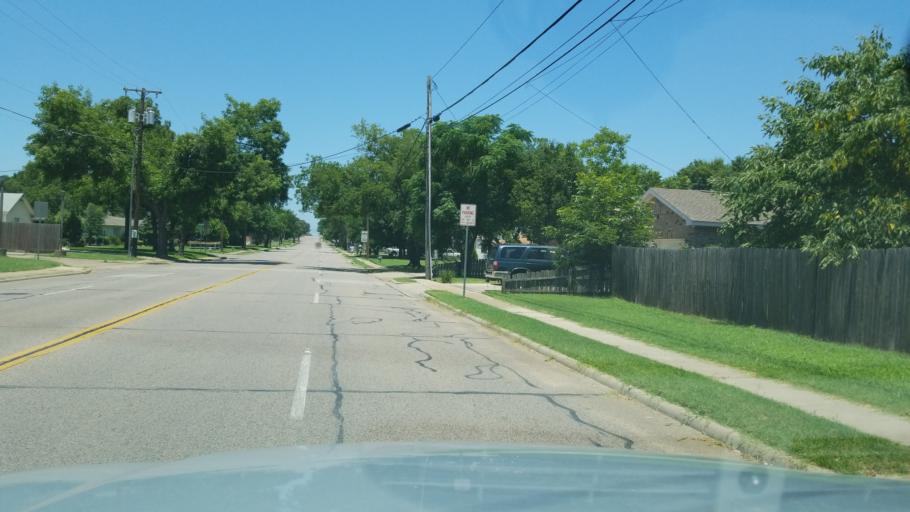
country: US
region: Texas
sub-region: Dallas County
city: Irving
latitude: 32.8014
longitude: -96.9257
